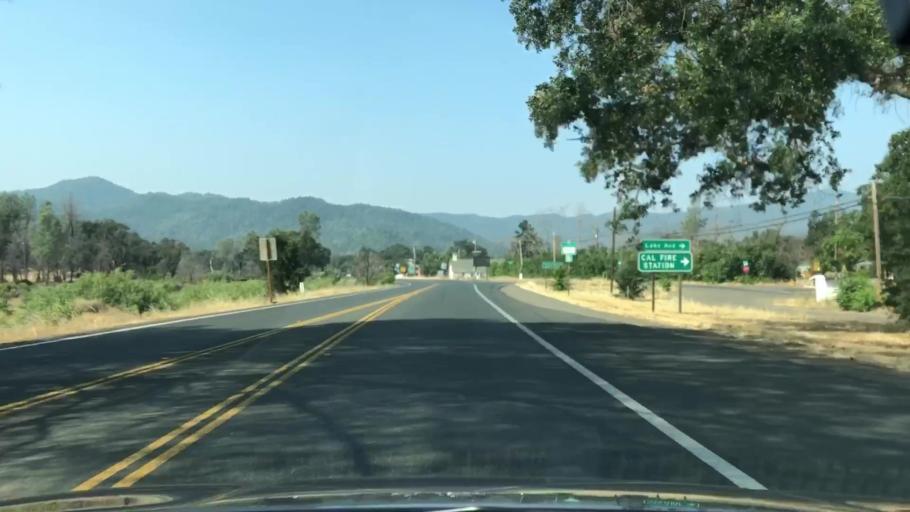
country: US
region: California
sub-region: Lake County
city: Middletown
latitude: 38.7474
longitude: -122.6182
